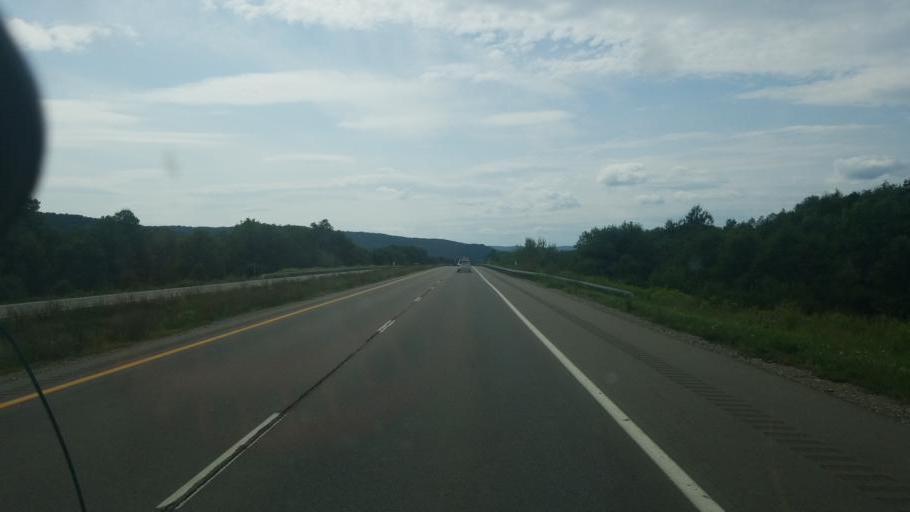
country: US
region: New York
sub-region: Cattaraugus County
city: Allegany
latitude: 42.0885
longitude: -78.5724
